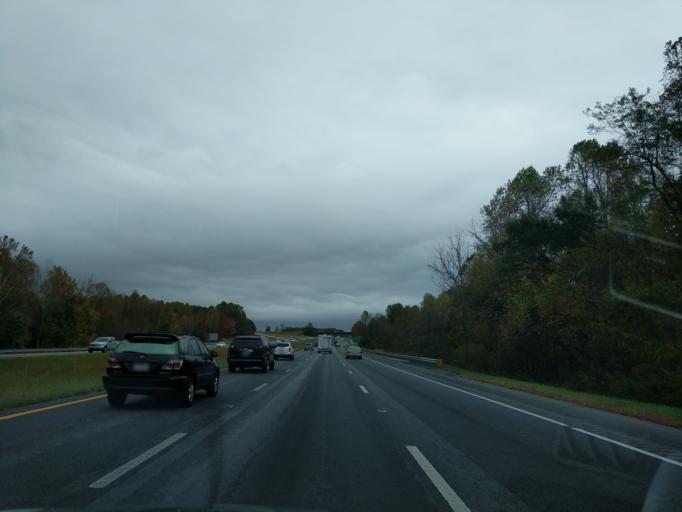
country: US
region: North Carolina
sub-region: Davidson County
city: Thomasville
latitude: 35.8624
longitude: -80.0445
